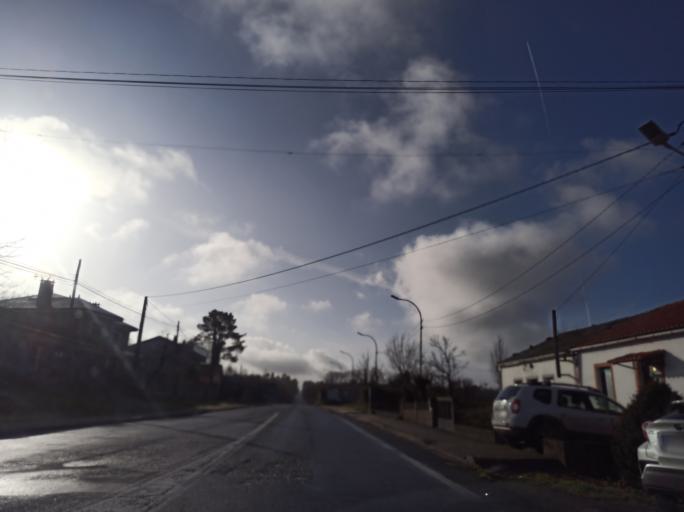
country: ES
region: Galicia
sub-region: Provincia da Coruna
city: Curtis
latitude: 43.1343
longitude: -8.0345
